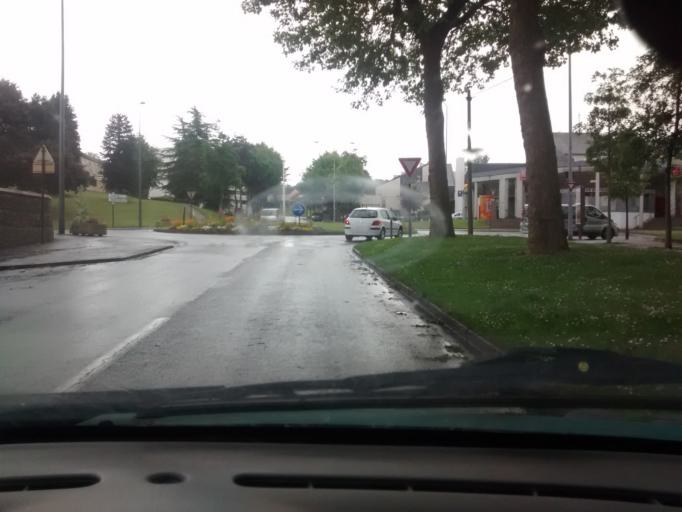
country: FR
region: Lower Normandy
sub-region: Departement de la Manche
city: Saint-Lo
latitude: 49.1121
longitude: -1.0703
